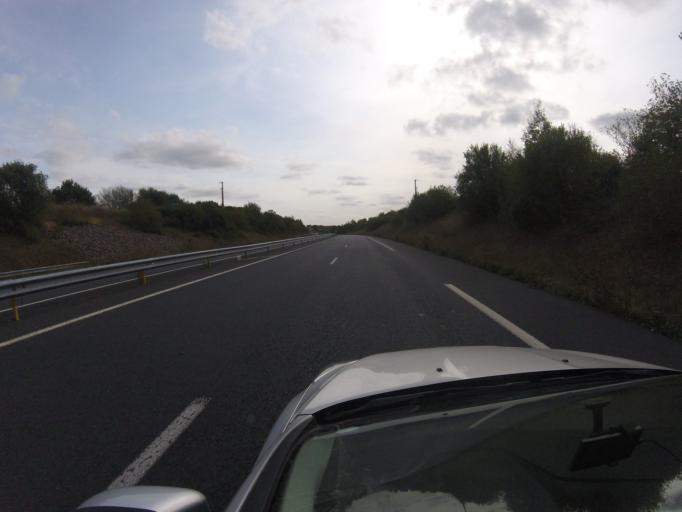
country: FR
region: Lower Normandy
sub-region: Departement de la Manche
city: Pont-Hebert
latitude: 49.1673
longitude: -1.1543
